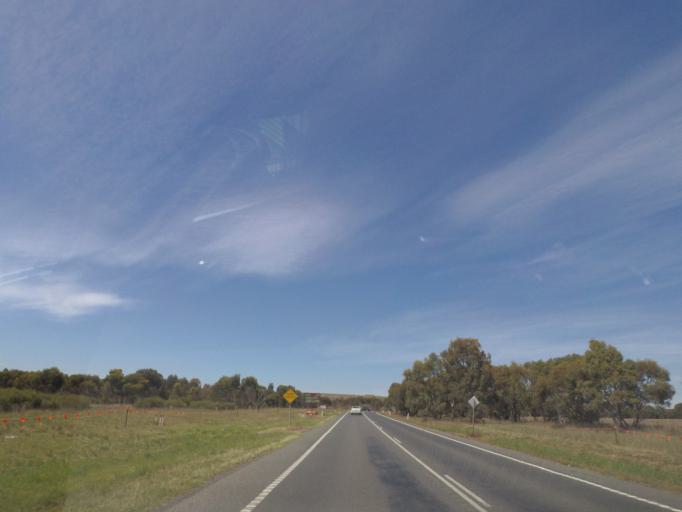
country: AU
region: Victoria
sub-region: Greater Geelong
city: Lara
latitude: -37.8829
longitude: 144.3785
